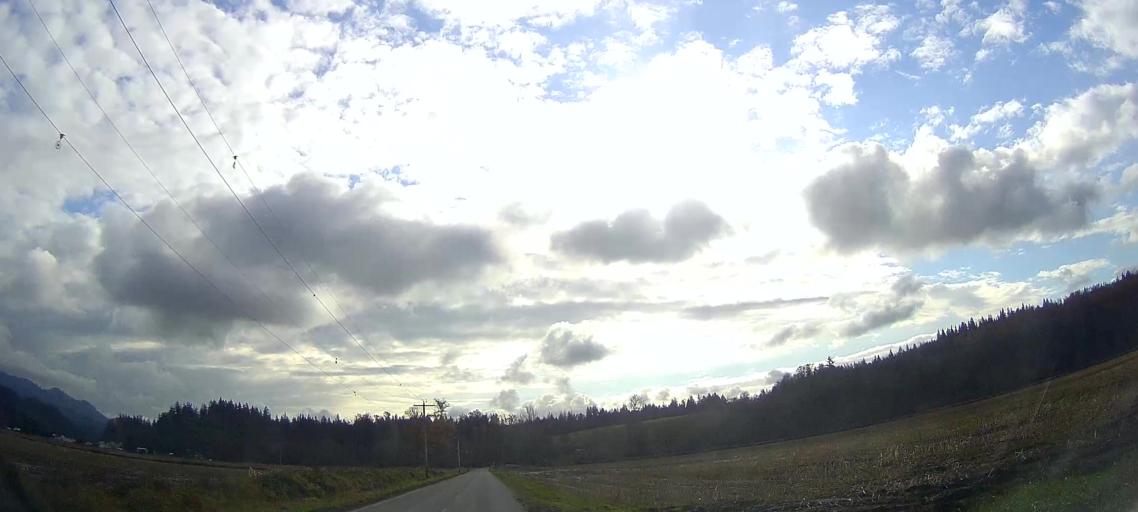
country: US
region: Washington
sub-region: Skagit County
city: Big Lake
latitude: 48.4316
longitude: -122.2207
